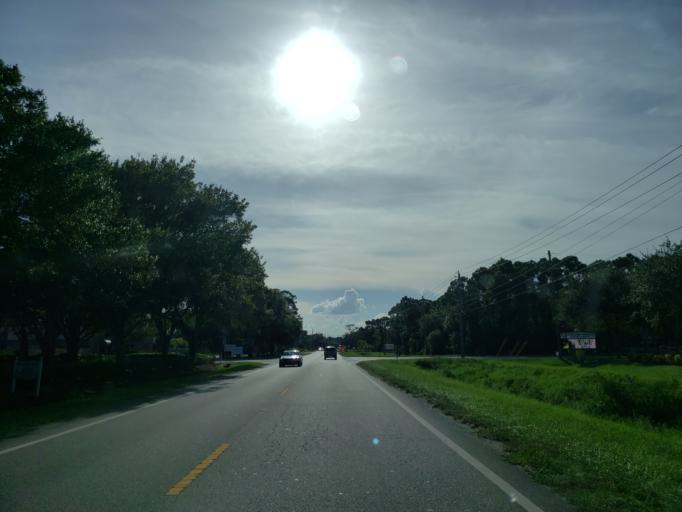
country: US
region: Florida
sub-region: Brevard County
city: June Park
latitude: 28.0992
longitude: -80.6856
